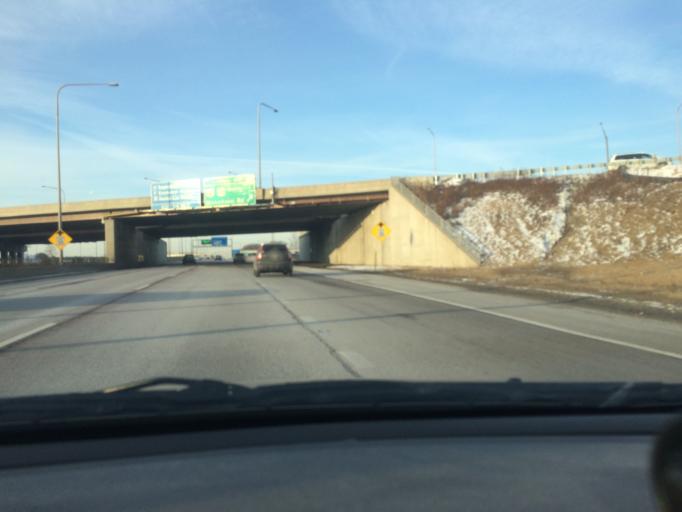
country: US
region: Illinois
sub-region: Cook County
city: Rosemont
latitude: 41.9815
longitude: -87.8780
